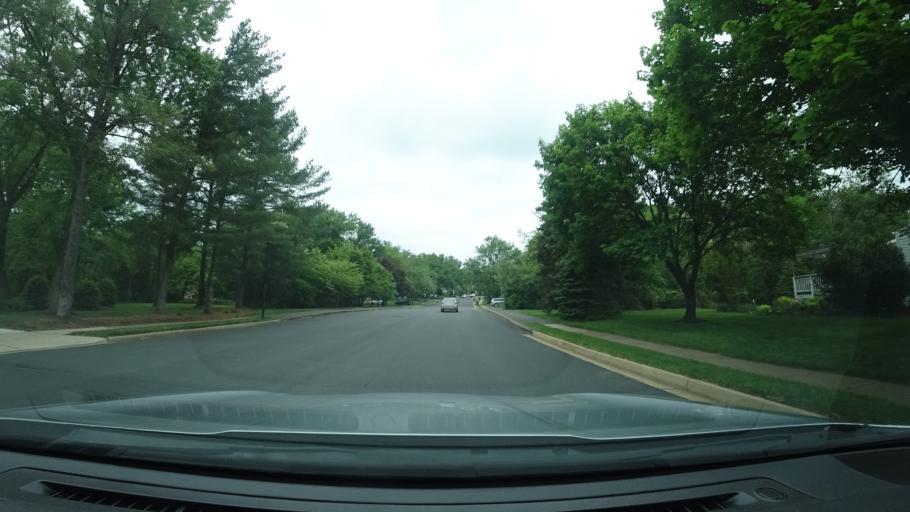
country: US
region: Virginia
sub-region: Fairfax County
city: Oak Hill
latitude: 38.9246
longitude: -77.3846
